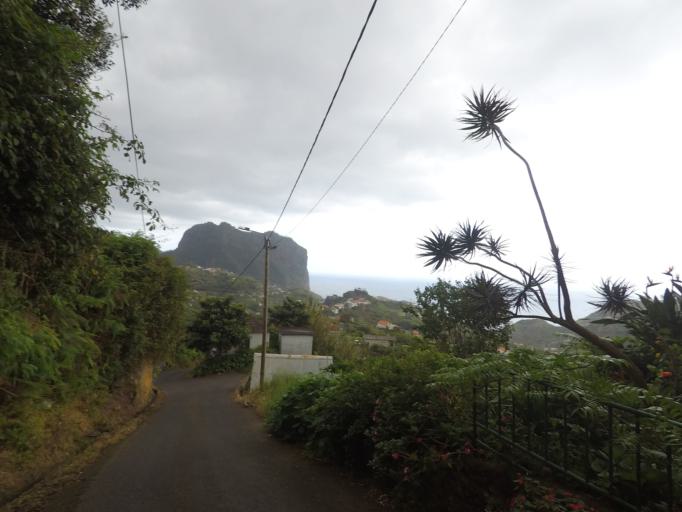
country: PT
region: Madeira
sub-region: Santana
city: Santana
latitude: 32.7546
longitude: -16.8273
